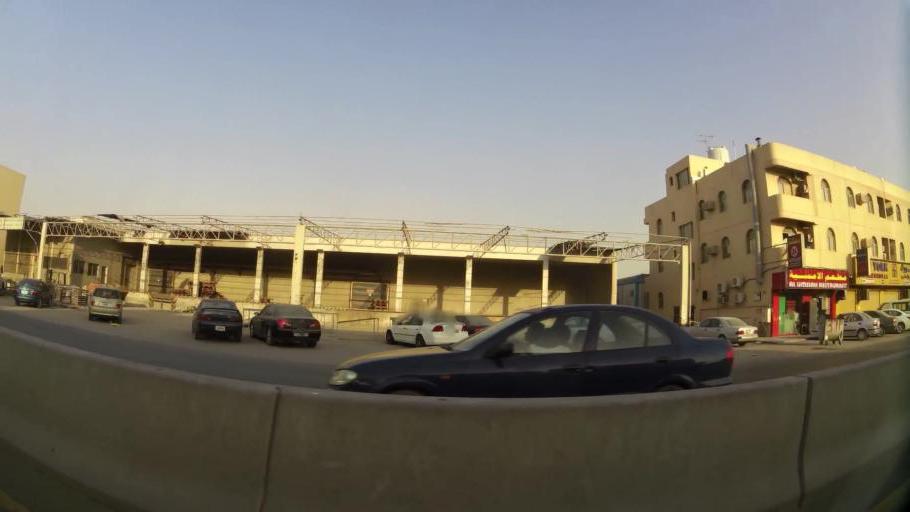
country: AE
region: Ash Shariqah
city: Sharjah
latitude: 25.3304
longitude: 55.4095
